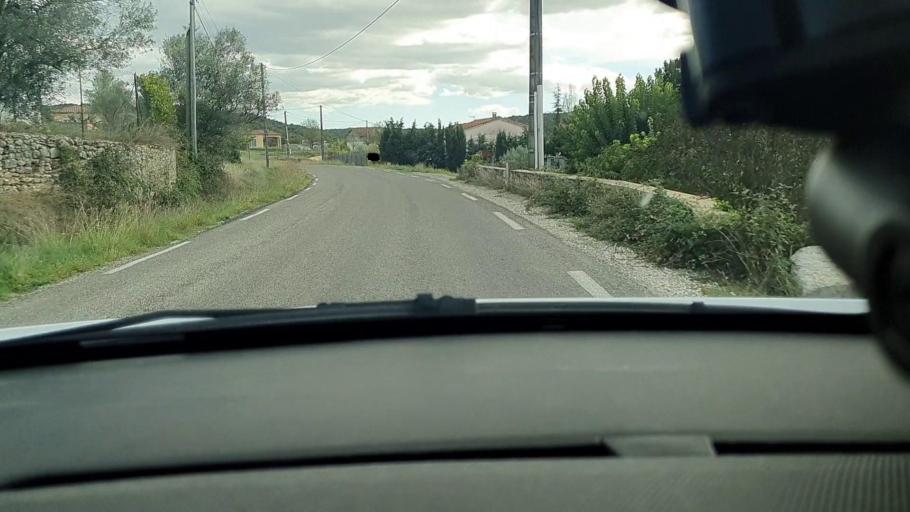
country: FR
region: Languedoc-Roussillon
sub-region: Departement du Gard
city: Les Mages
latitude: 44.2245
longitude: 4.1725
